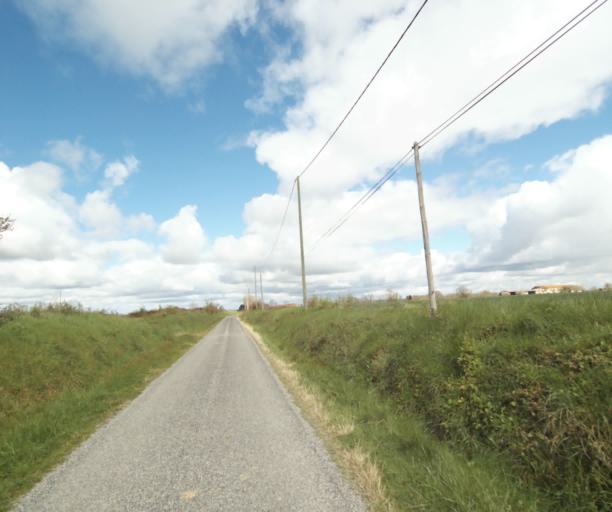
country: FR
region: Midi-Pyrenees
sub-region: Departement de l'Ariege
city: Saverdun
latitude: 43.2193
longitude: 1.5797
